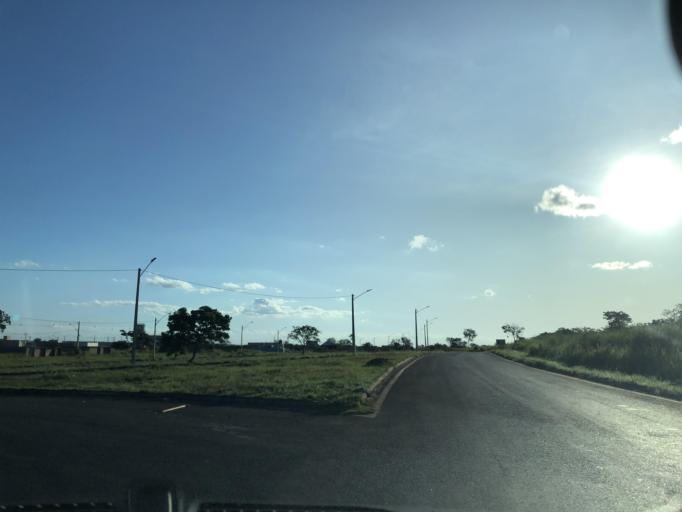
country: BR
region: Goias
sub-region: Luziania
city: Luziania
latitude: -16.2629
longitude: -47.9714
